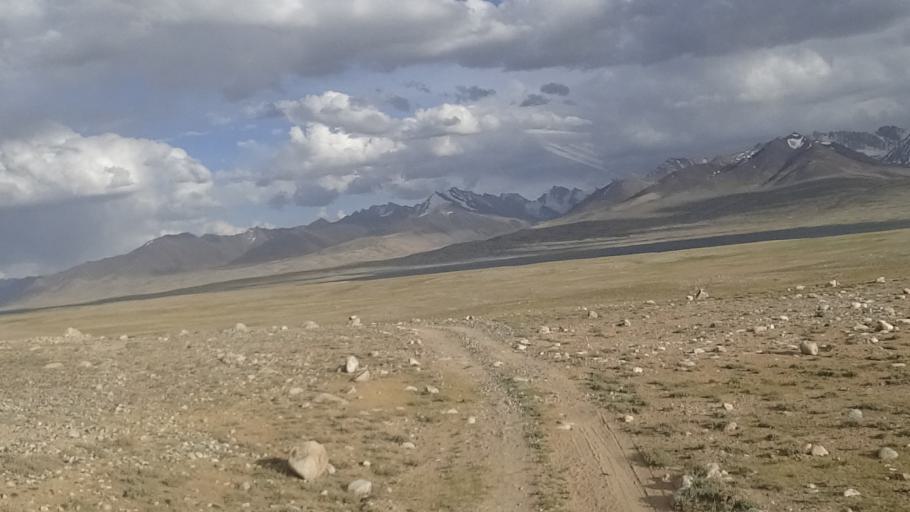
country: TJ
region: Gorno-Badakhshan
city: Murghob
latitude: 37.4628
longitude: 73.6149
